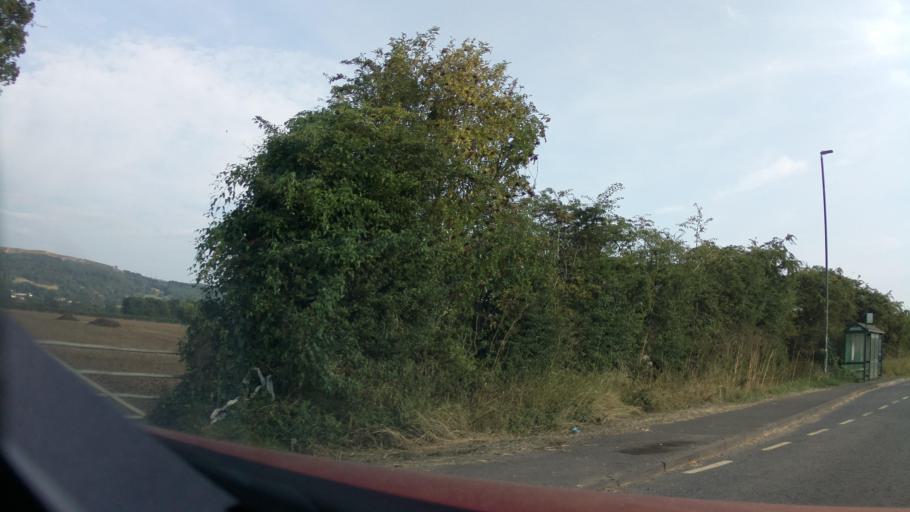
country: GB
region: England
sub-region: Gloucestershire
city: Gotherington
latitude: 51.9368
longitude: -2.0654
